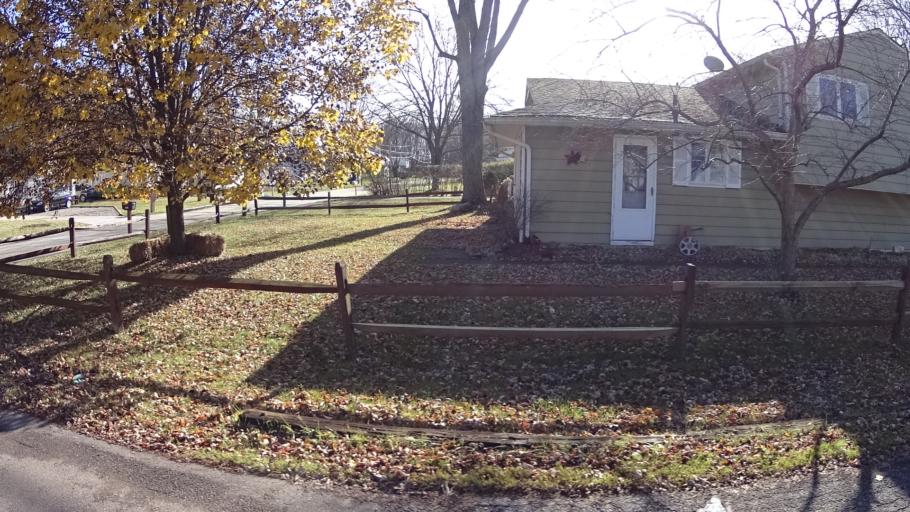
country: US
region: Ohio
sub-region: Lorain County
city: North Ridgeville
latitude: 41.4080
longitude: -81.9860
